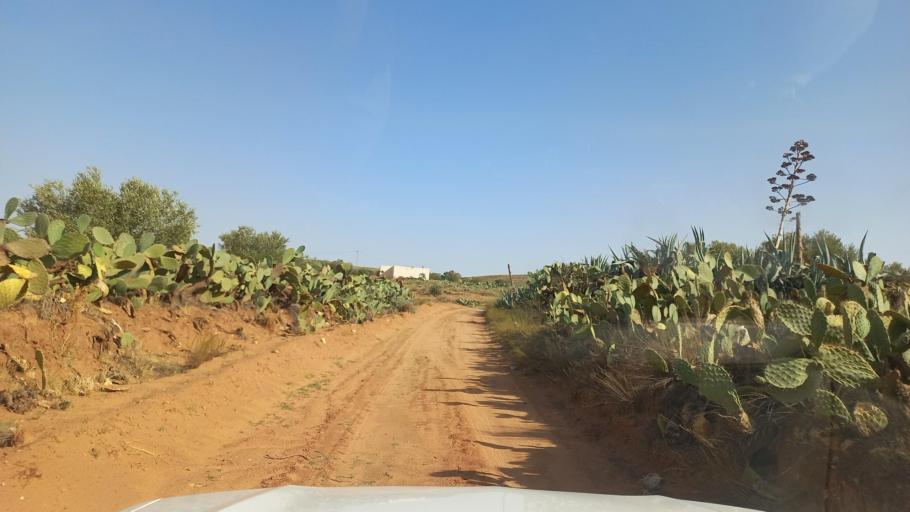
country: TN
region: Al Qasrayn
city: Kasserine
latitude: 35.2016
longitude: 8.9656
